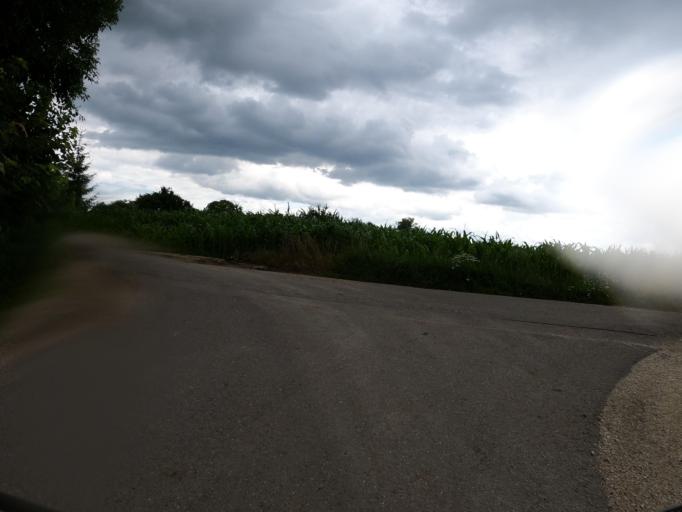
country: DE
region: Baden-Wuerttemberg
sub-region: Tuebingen Region
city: Langenau
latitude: 48.4816
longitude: 10.1078
